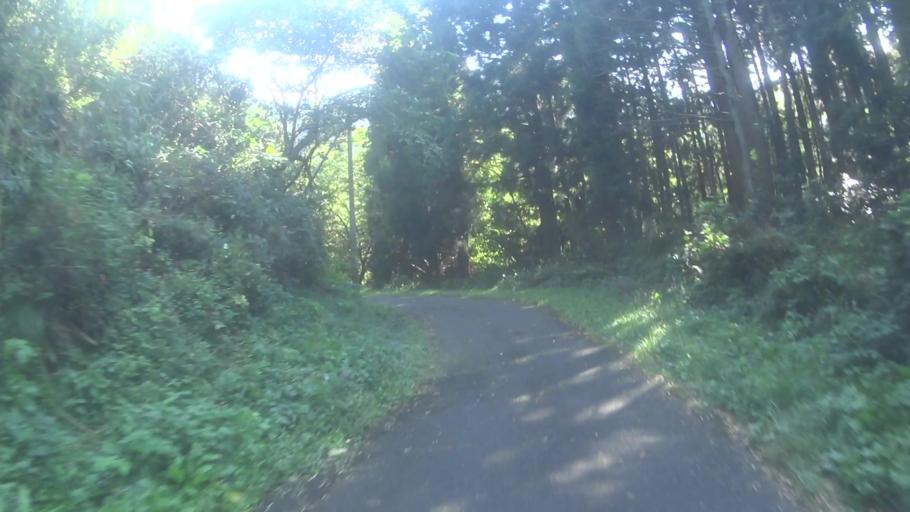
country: JP
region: Kyoto
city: Miyazu
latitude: 35.7161
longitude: 135.1654
